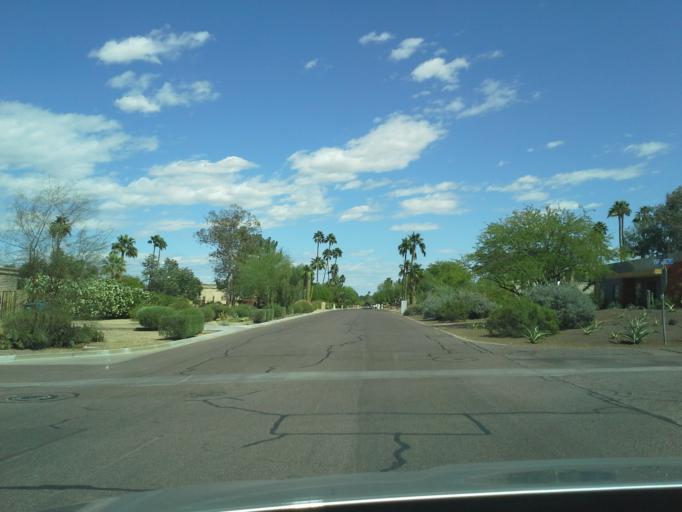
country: US
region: Arizona
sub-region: Maricopa County
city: Paradise Valley
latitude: 33.5750
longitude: -111.9492
